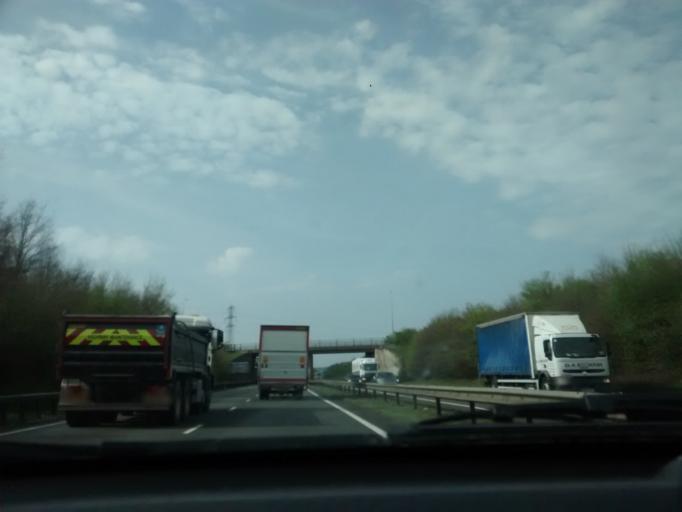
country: GB
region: England
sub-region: Oxfordshire
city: Kidlington
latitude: 51.8050
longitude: -1.2745
